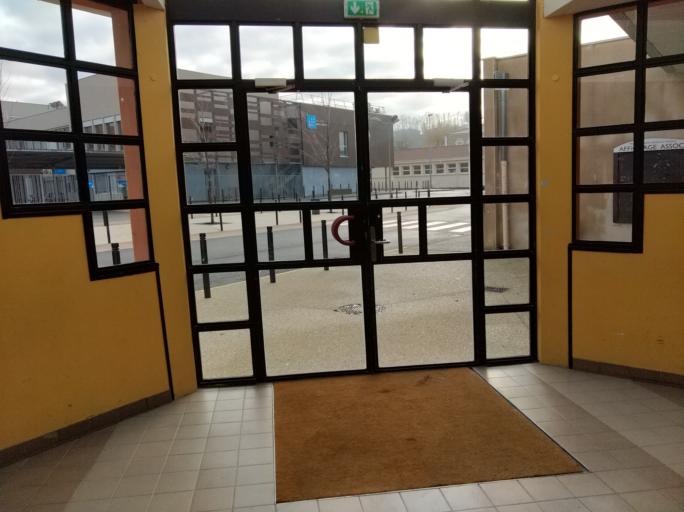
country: FR
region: Rhone-Alpes
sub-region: Departement de la Drome
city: Saint-Sorlin-en-Valloire
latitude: 45.2898
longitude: 4.9492
